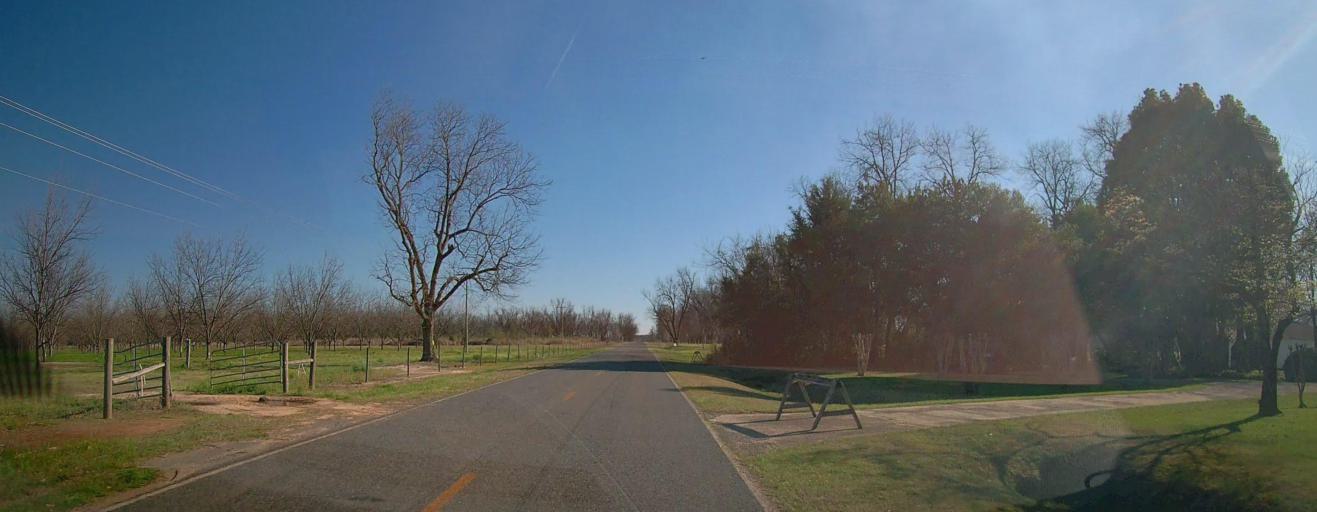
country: US
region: Georgia
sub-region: Peach County
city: Fort Valley
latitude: 32.6071
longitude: -83.8522
